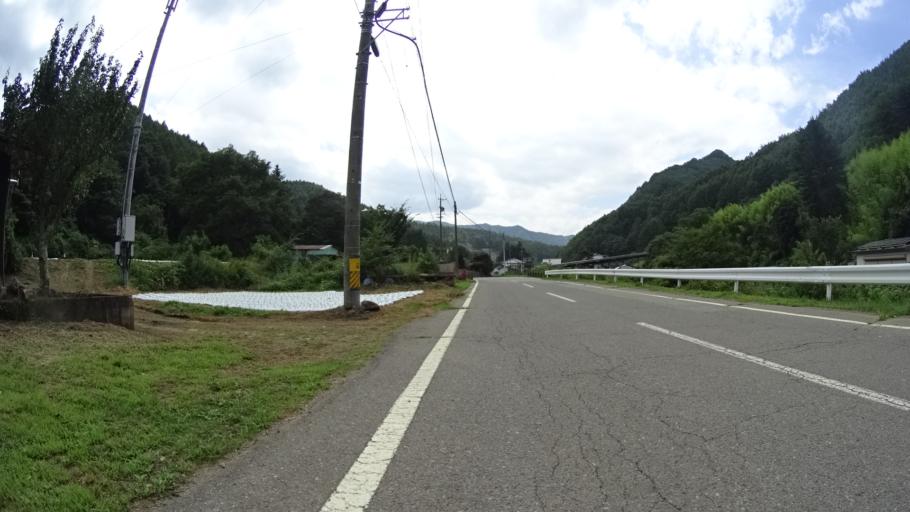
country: JP
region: Nagano
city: Saku
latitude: 36.0646
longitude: 138.5884
